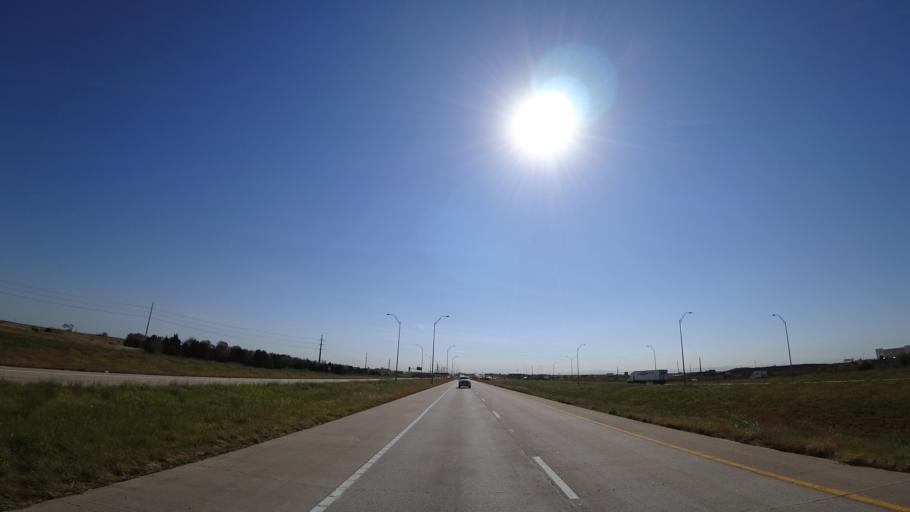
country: US
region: Texas
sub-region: Travis County
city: Pflugerville
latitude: 30.4198
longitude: -97.5867
